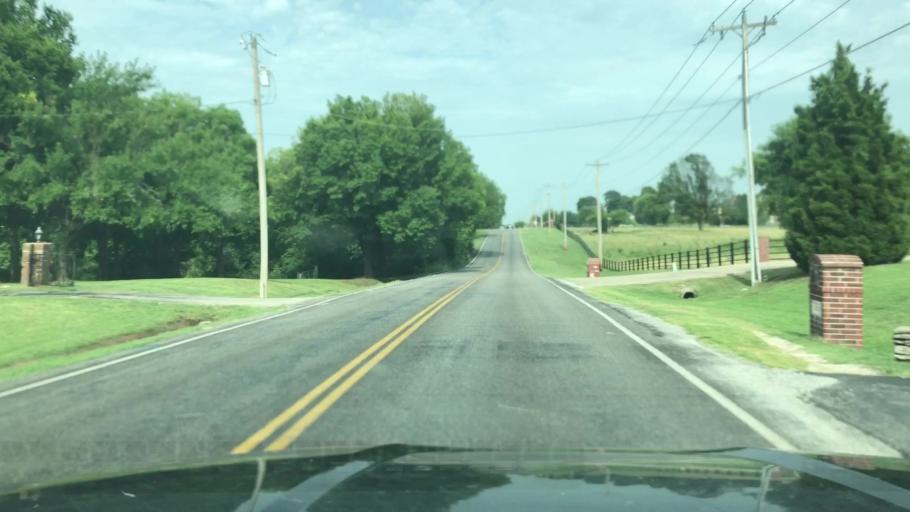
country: US
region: Oklahoma
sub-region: Tulsa County
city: Oakhurst
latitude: 36.0902
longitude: -96.0958
